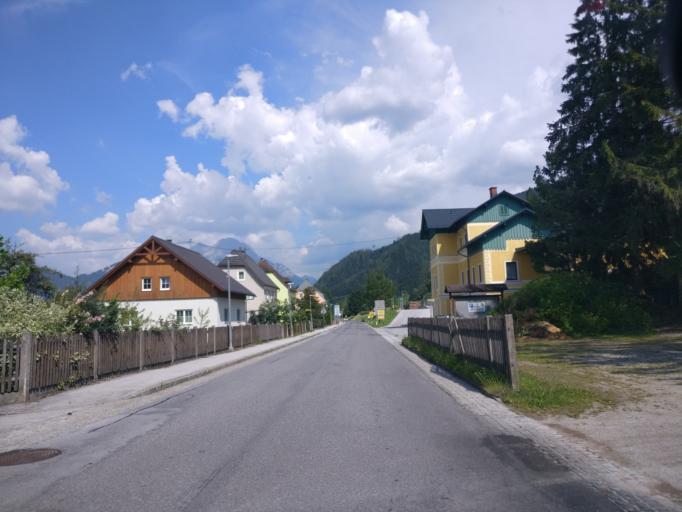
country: AT
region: Styria
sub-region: Politischer Bezirk Liezen
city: Admont
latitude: 47.5737
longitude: 14.4675
